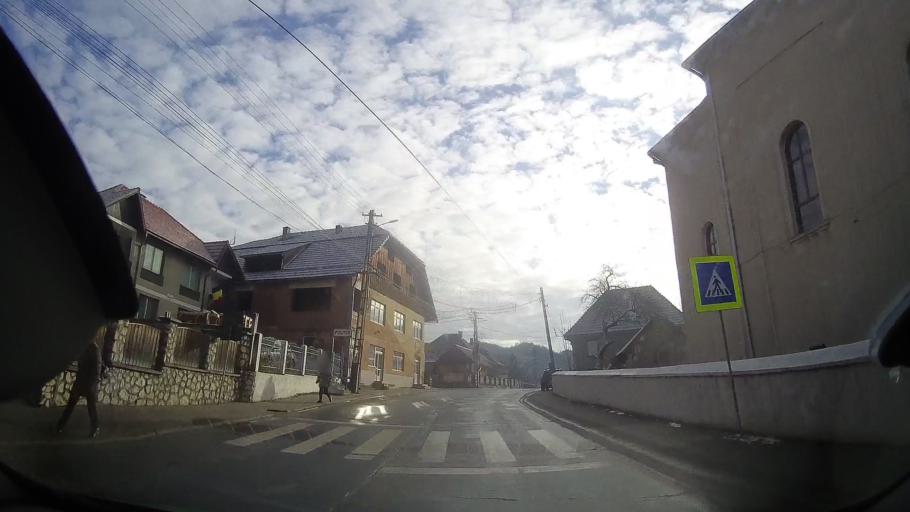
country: RO
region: Alba
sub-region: Comuna Bistra
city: Bistra
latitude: 46.3771
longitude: 23.1020
